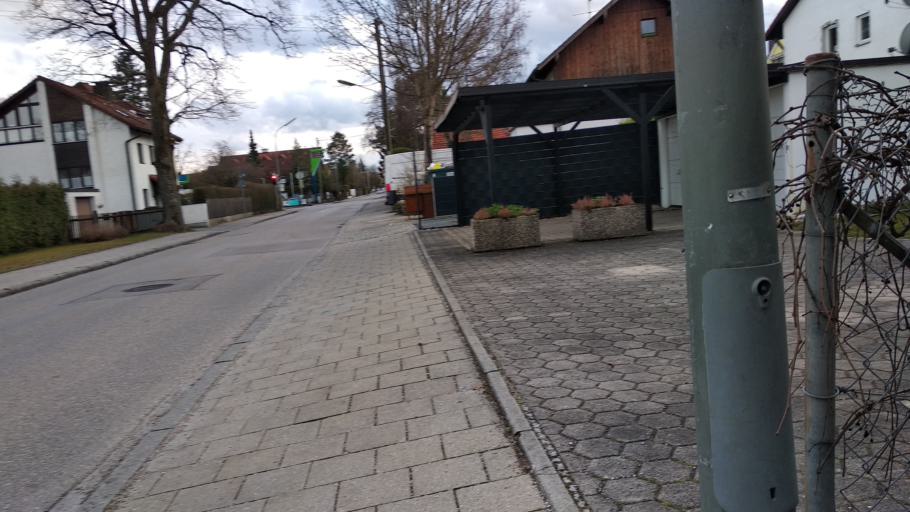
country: DE
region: Bavaria
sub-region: Upper Bavaria
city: Ottobrunn
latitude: 48.0754
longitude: 11.6769
